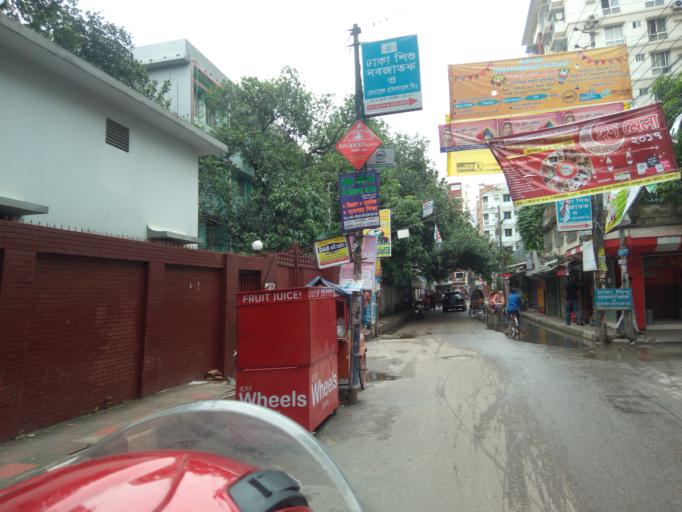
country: BD
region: Dhaka
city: Azimpur
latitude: 23.7558
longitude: 90.3677
